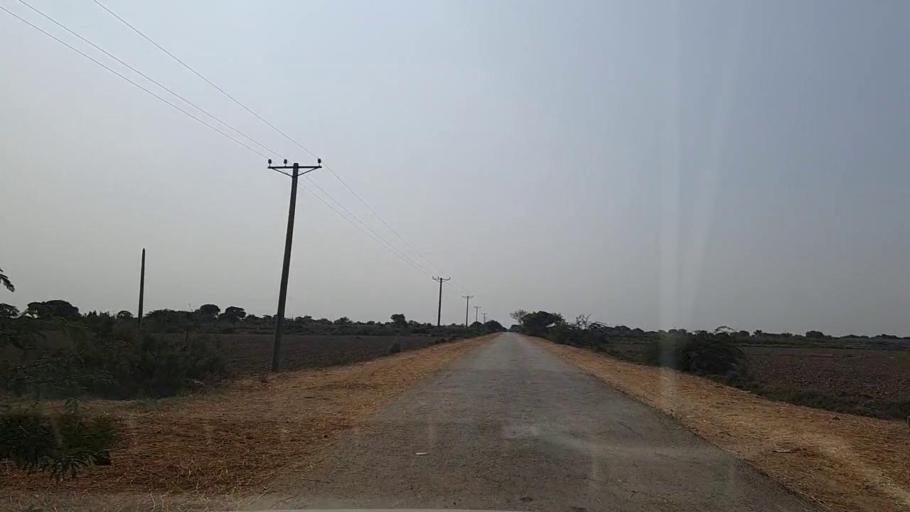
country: PK
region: Sindh
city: Chuhar Jamali
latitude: 24.2789
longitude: 67.9183
